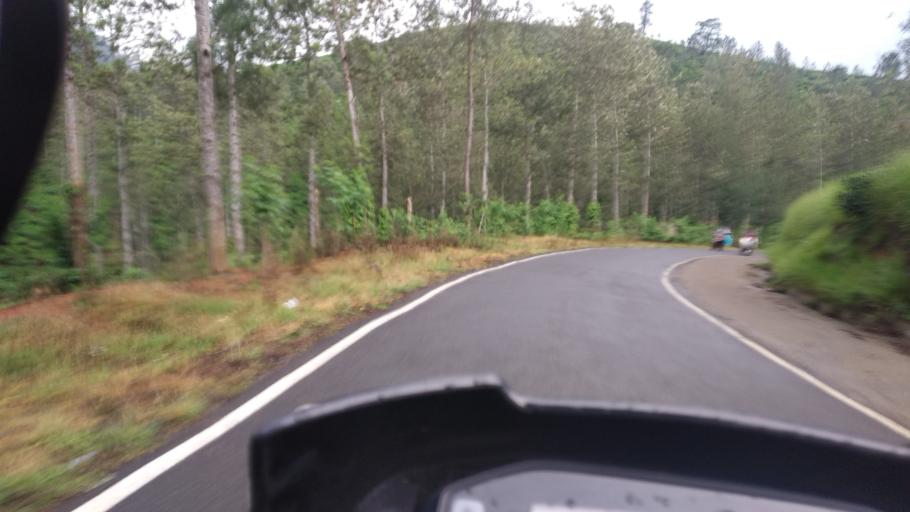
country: IN
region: Tamil Nadu
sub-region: Theni
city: Gudalur
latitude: 9.5677
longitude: 77.0826
